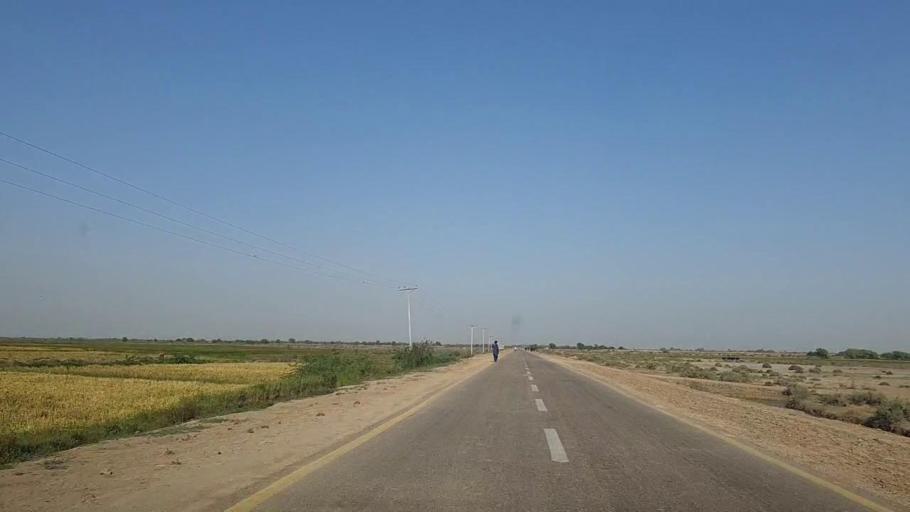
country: PK
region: Sindh
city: Jati
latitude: 24.4552
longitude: 68.3423
